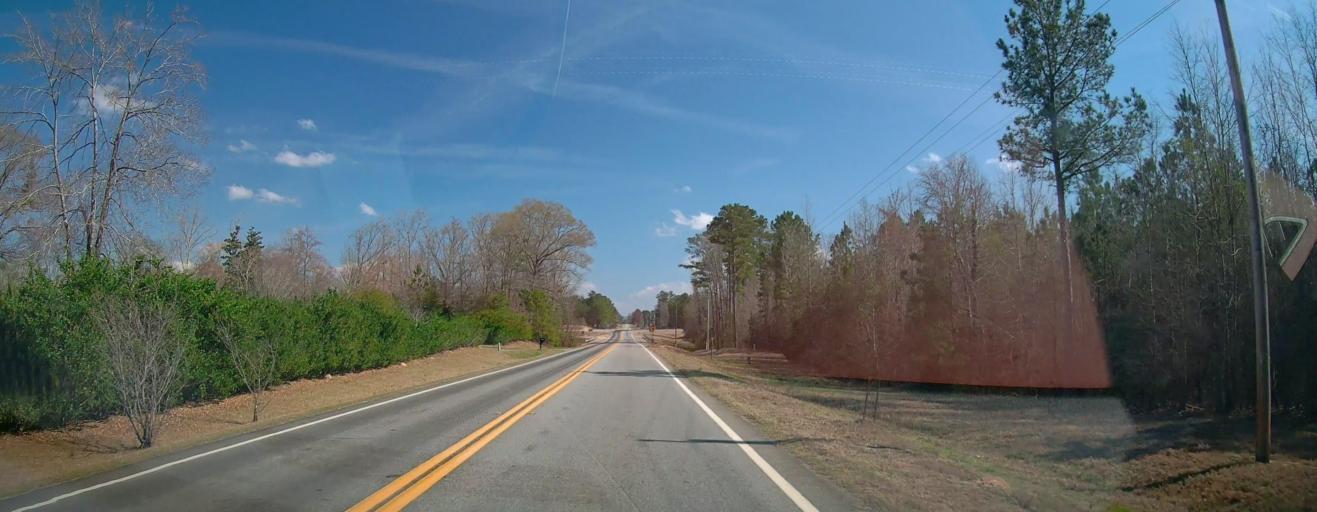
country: US
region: Georgia
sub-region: Wilkinson County
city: Gordon
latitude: 32.8961
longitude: -83.3631
